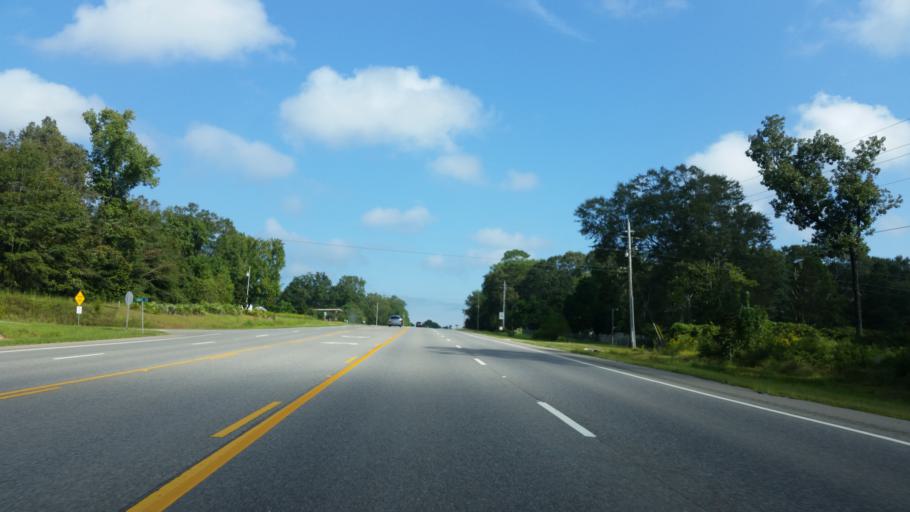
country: US
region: Alabama
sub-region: Baldwin County
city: Bay Minette
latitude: 30.9537
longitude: -87.7613
